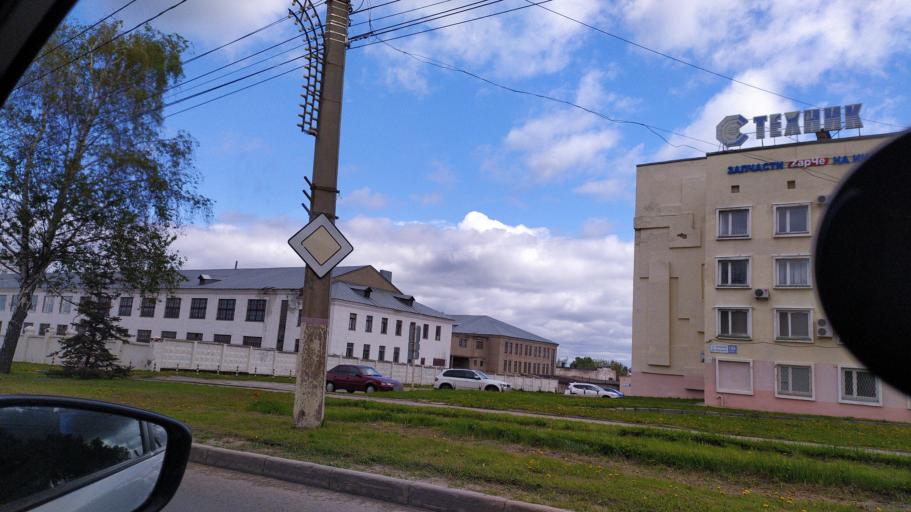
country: RU
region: Chuvashia
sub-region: Cheboksarskiy Rayon
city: Cheboksary
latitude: 56.1328
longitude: 47.2835
